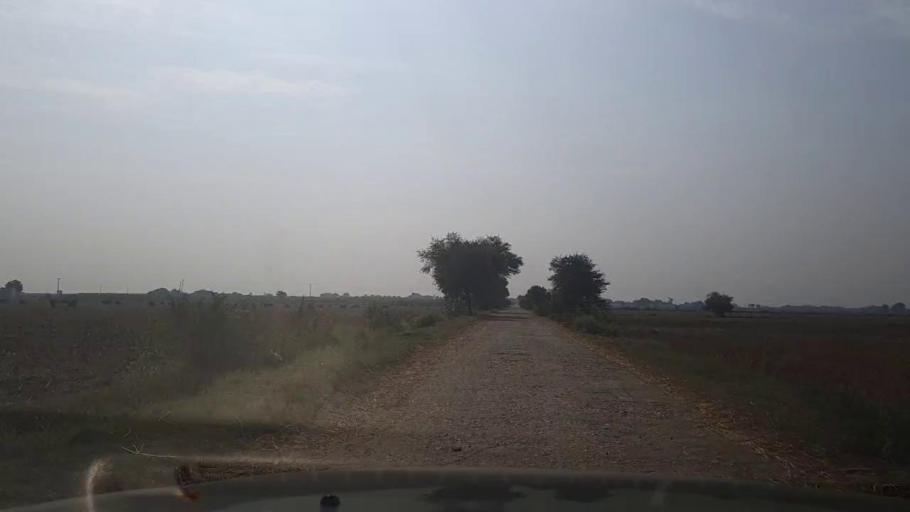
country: PK
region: Sindh
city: Bulri
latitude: 25.0164
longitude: 68.2996
